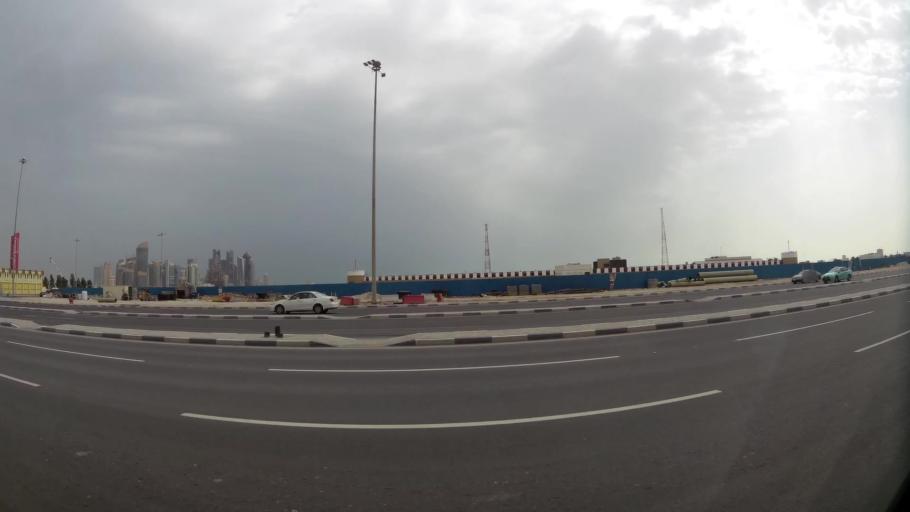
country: QA
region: Baladiyat ad Dawhah
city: Doha
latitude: 25.3005
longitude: 51.5072
